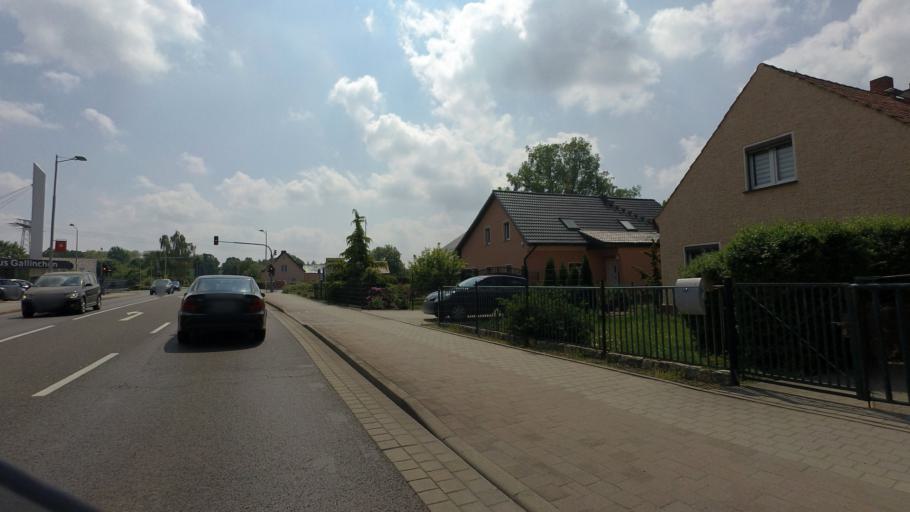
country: DE
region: Brandenburg
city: Cottbus
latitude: 51.7087
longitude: 14.3575
